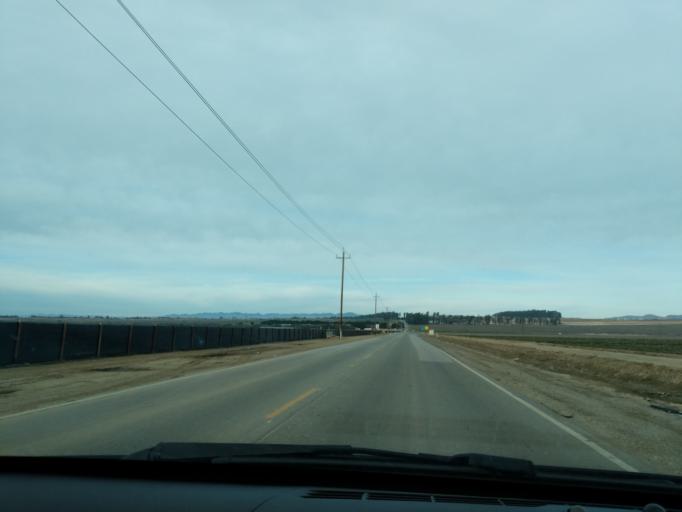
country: US
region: California
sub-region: Santa Barbara County
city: Guadalupe
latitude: 35.0075
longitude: -120.5689
